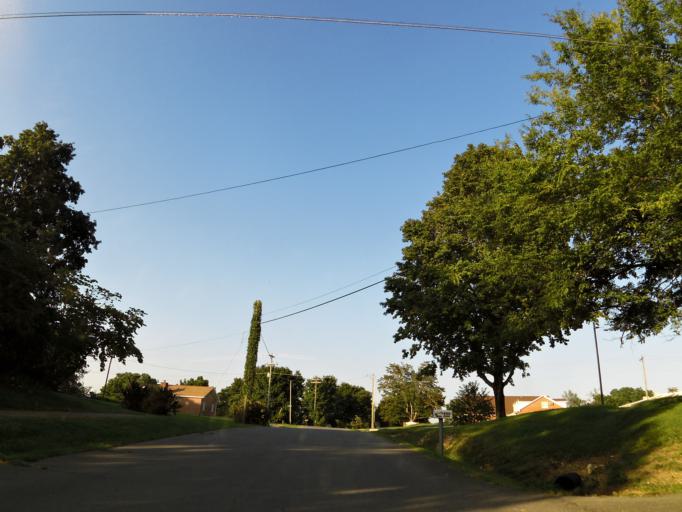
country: US
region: Tennessee
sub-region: McMinn County
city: Athens
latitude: 35.4544
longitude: -84.5991
